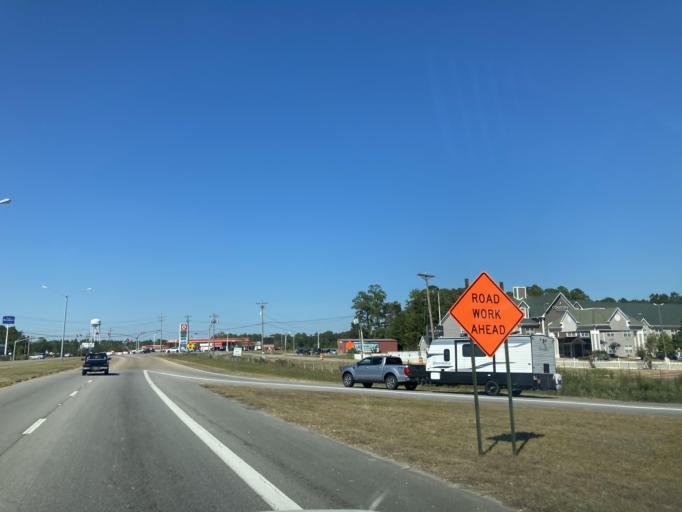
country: US
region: Mississippi
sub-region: Jackson County
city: Gulf Hills
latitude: 30.4558
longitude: -88.8431
